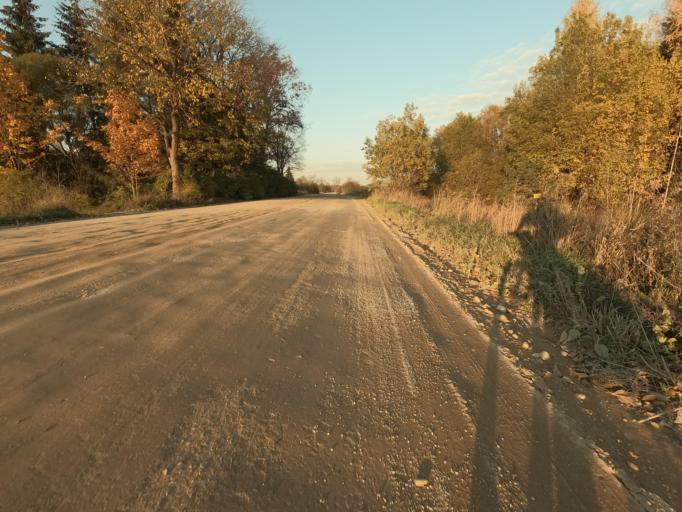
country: RU
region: Leningrad
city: Lyuban'
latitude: 59.0229
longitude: 31.0982
